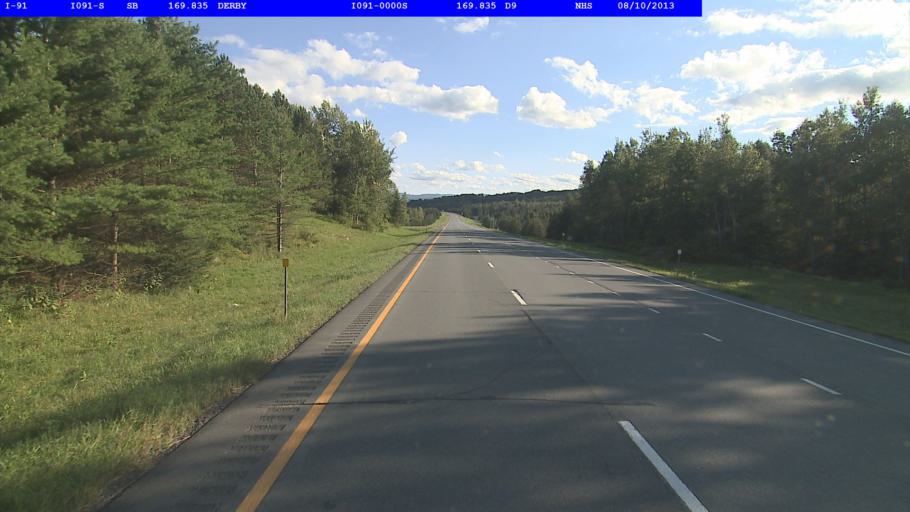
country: US
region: Vermont
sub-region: Orleans County
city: Newport
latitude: 44.9198
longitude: -72.1749
